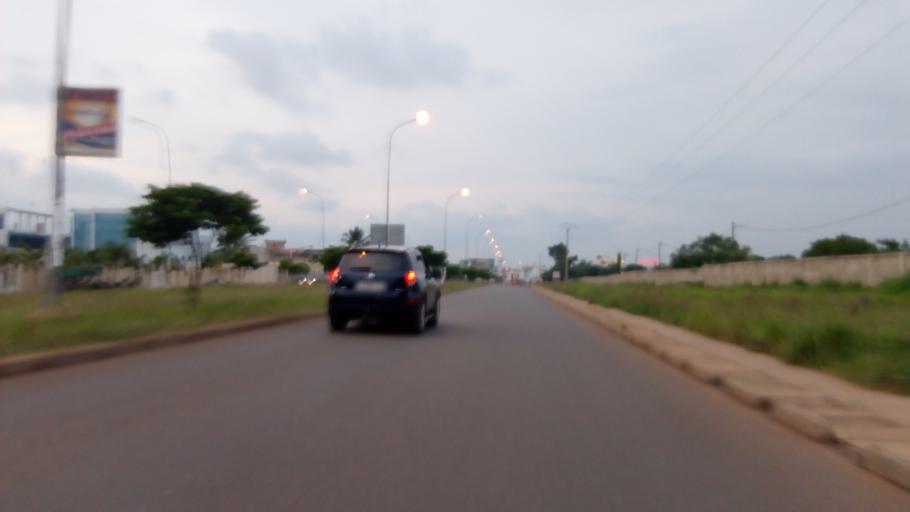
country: TG
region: Maritime
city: Lome
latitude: 6.2075
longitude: 1.1933
